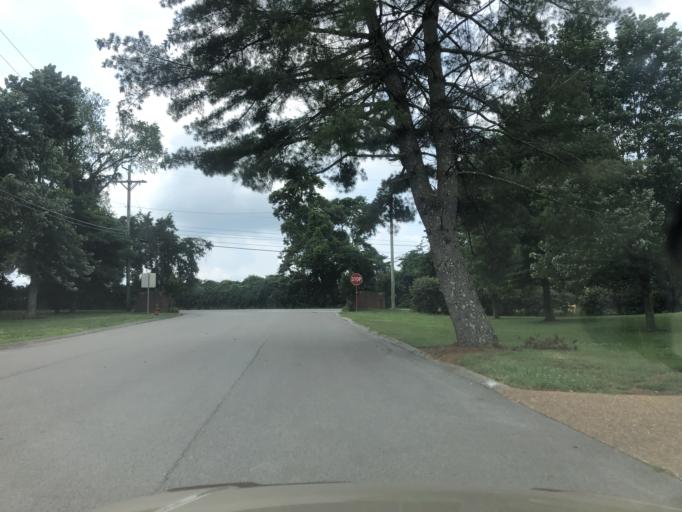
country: US
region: Tennessee
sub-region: Davidson County
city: Lakewood
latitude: 36.2316
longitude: -86.6111
